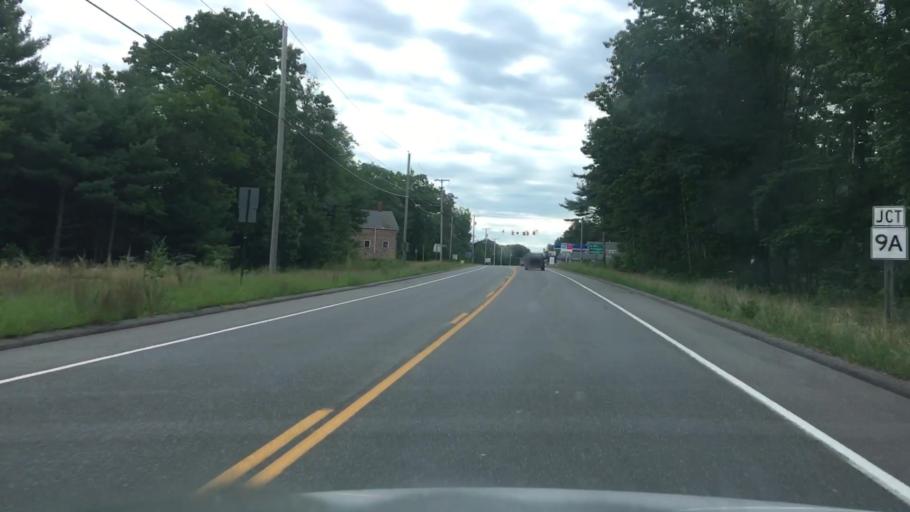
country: US
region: Maine
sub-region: York County
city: Wells Beach Station
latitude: 43.3331
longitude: -70.6274
